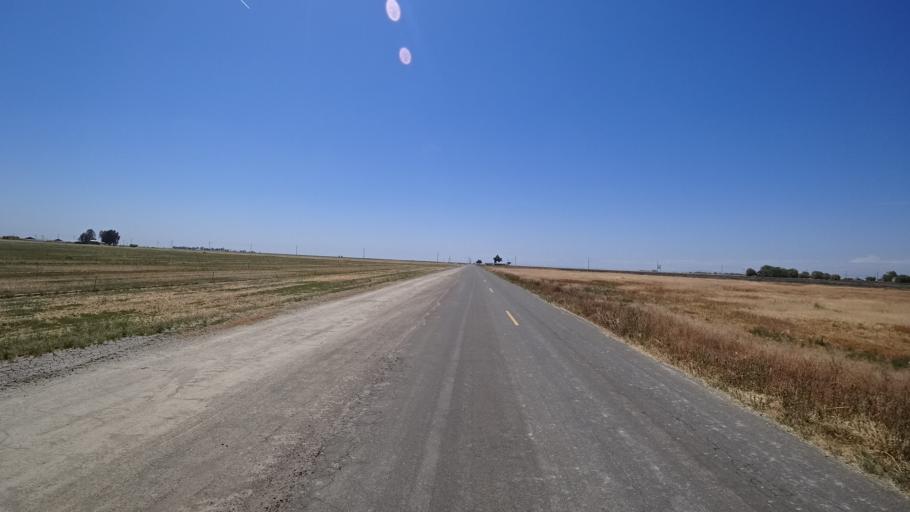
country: US
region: California
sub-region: Kings County
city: Armona
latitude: 36.2301
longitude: -119.7266
